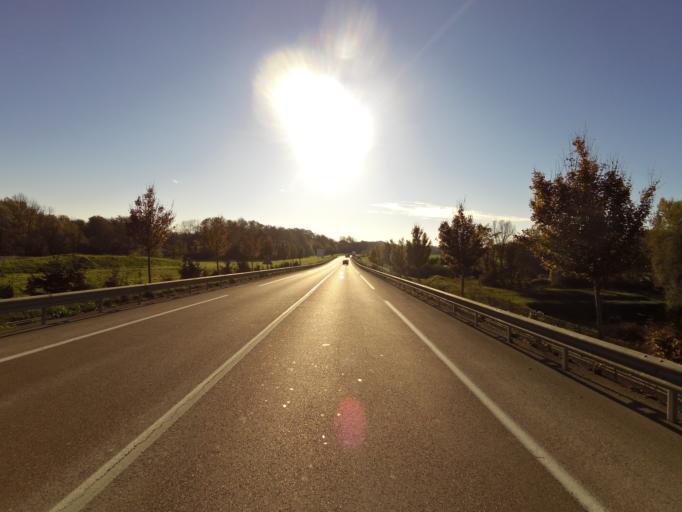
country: FR
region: Champagne-Ardenne
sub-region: Departement de l'Aube
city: Bucheres
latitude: 48.2497
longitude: 4.1132
